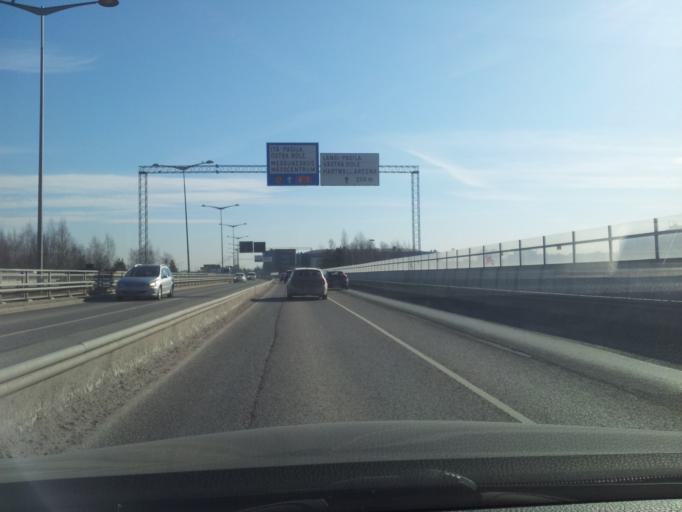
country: FI
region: Uusimaa
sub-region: Helsinki
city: Helsinki
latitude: 60.2077
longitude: 24.9212
